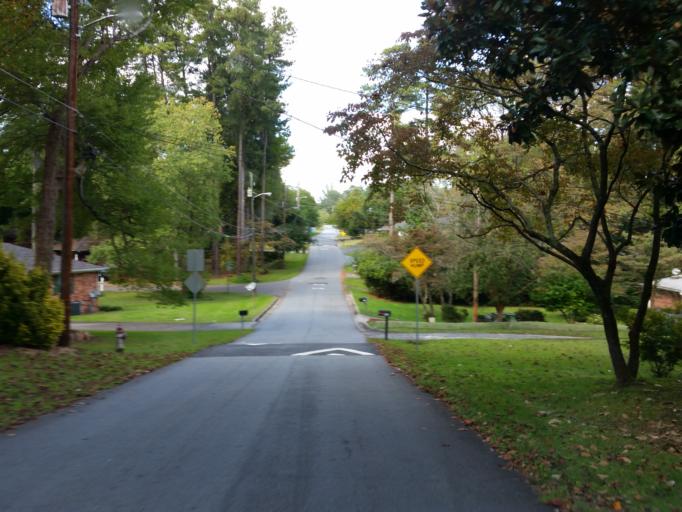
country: US
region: Georgia
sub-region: Cobb County
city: Marietta
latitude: 33.9463
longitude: -84.4936
